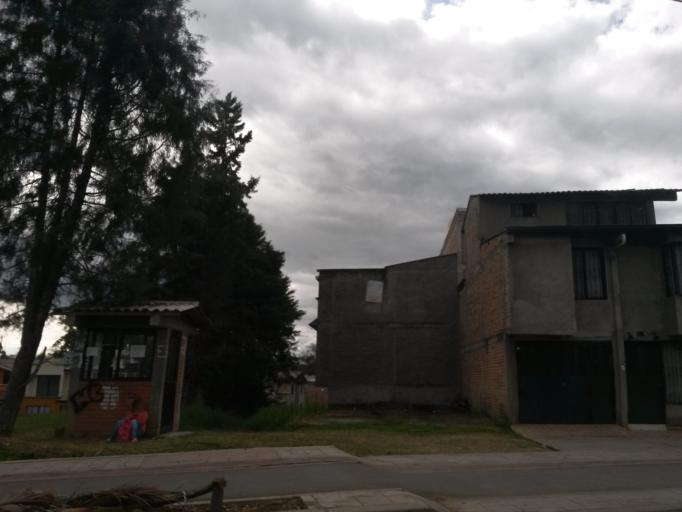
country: CO
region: Cauca
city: Popayan
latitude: 2.4501
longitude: -76.5927
